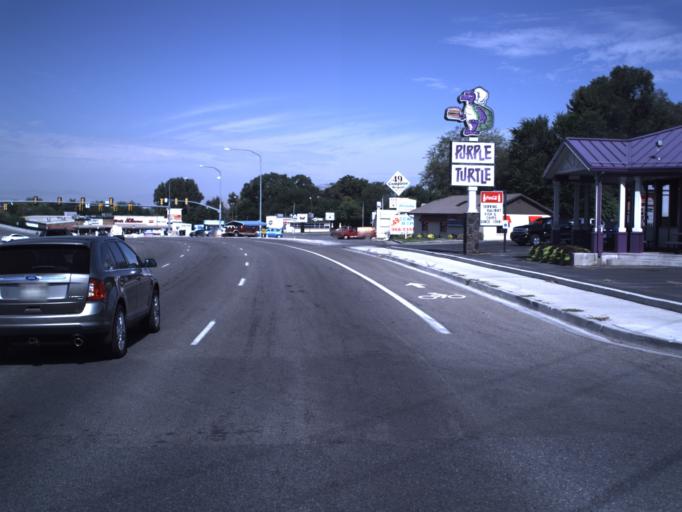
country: US
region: Utah
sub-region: Utah County
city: Pleasant Grove
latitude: 40.3582
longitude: -111.7390
